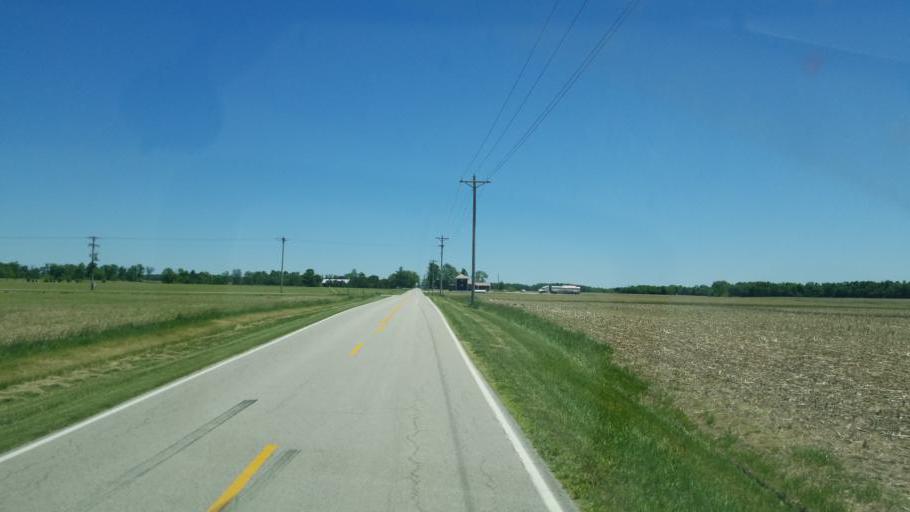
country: US
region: Ohio
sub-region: Darke County
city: Ansonia
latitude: 40.2648
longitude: -84.6769
